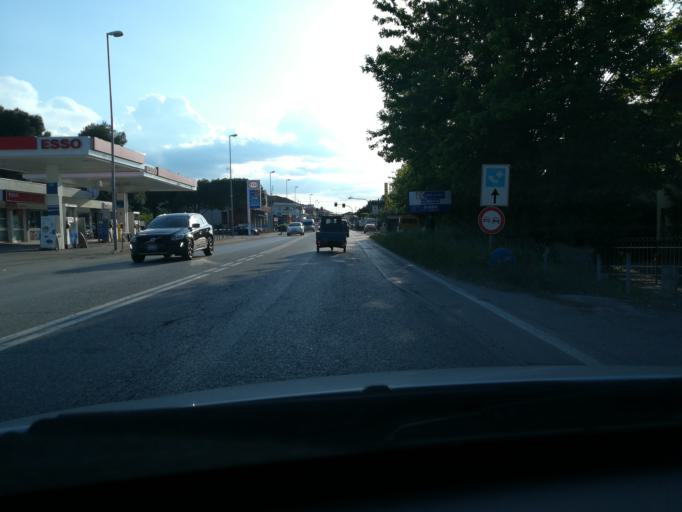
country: IT
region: Emilia-Romagna
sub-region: Provincia di Rimini
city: Riccione
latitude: 43.9926
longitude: 12.6597
